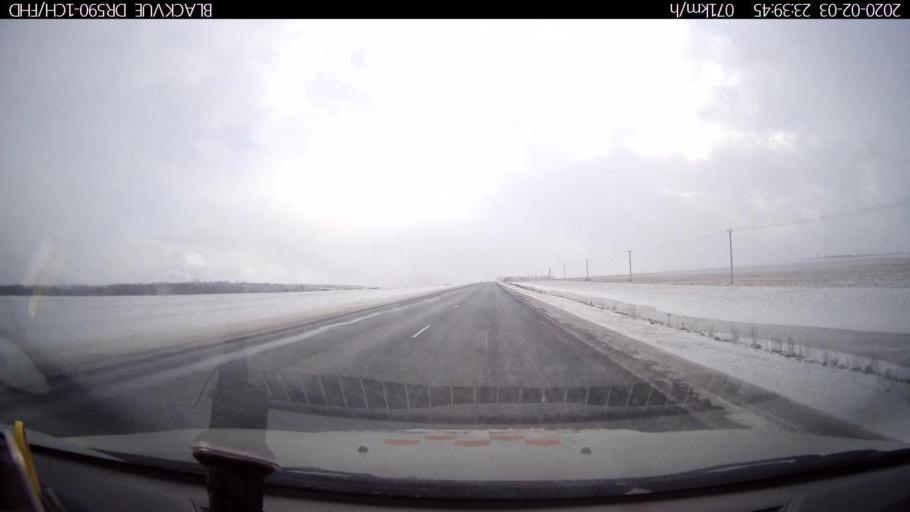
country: RU
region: Nizjnij Novgorod
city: Dal'neye Konstantinovo
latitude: 55.8806
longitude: 44.1373
